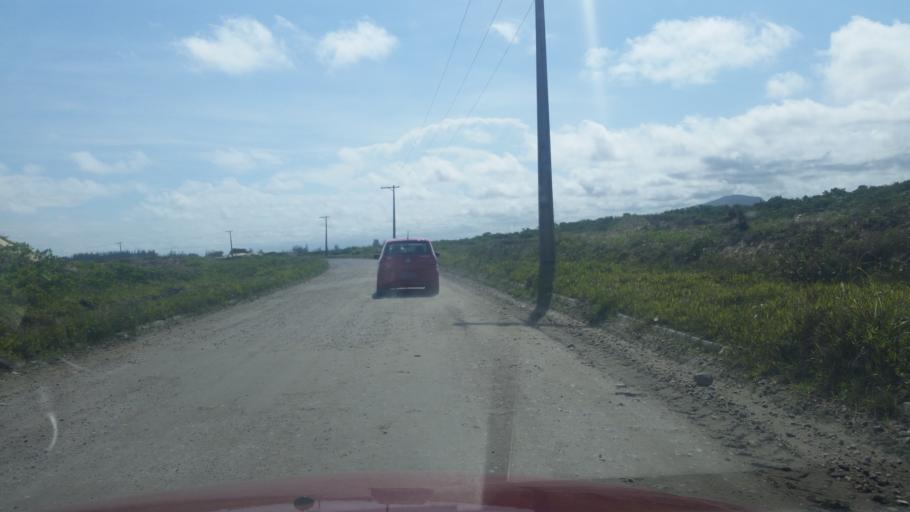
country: BR
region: Sao Paulo
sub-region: Iguape
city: Iguape
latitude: -24.7024
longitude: -47.4680
